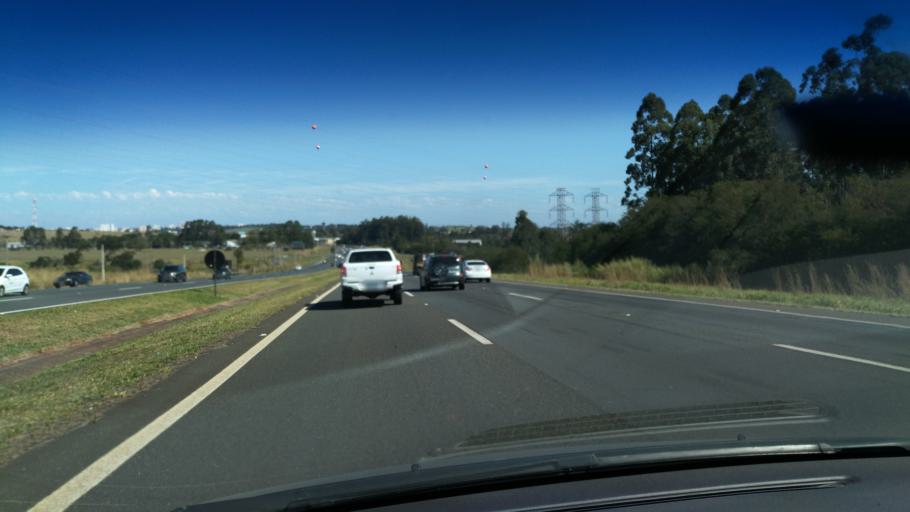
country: BR
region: Sao Paulo
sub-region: Jaguariuna
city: Jaguariuna
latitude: -22.7808
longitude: -47.0257
